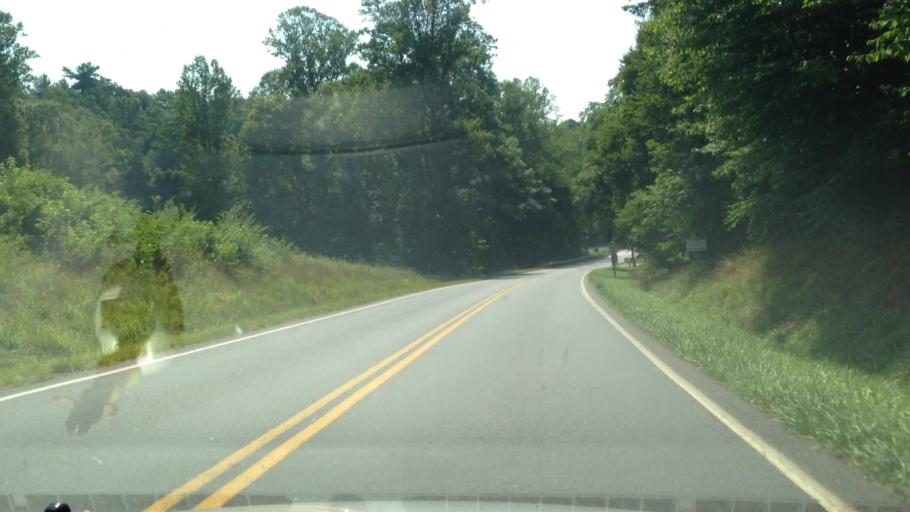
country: US
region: Virginia
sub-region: Patrick County
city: Stuart
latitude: 36.5906
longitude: -80.4119
